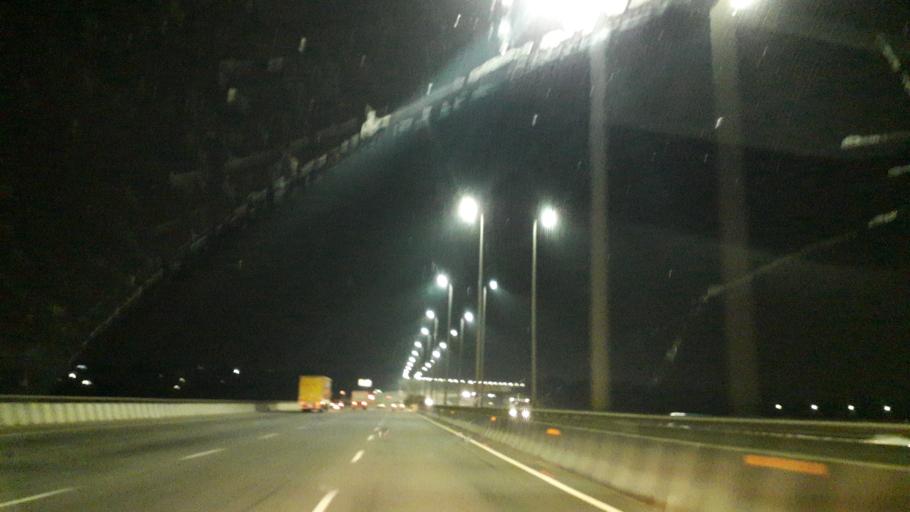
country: IN
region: Telangana
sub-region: Hyderabad
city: Hyderabad
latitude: 17.3286
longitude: 78.3727
